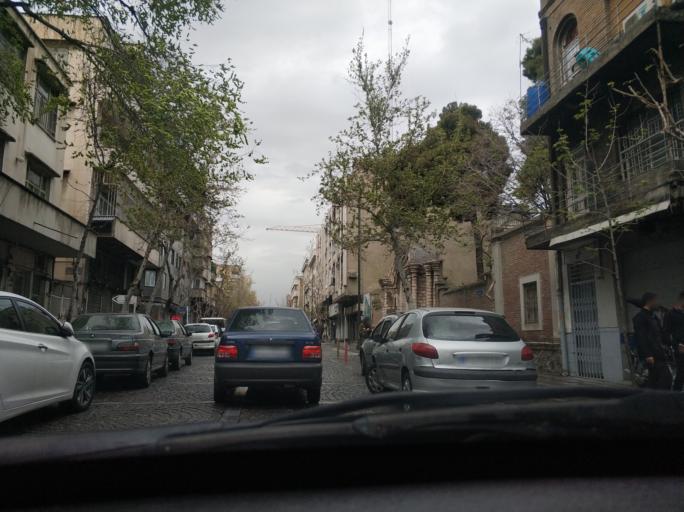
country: IR
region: Tehran
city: Tehran
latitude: 35.6931
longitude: 51.4143
